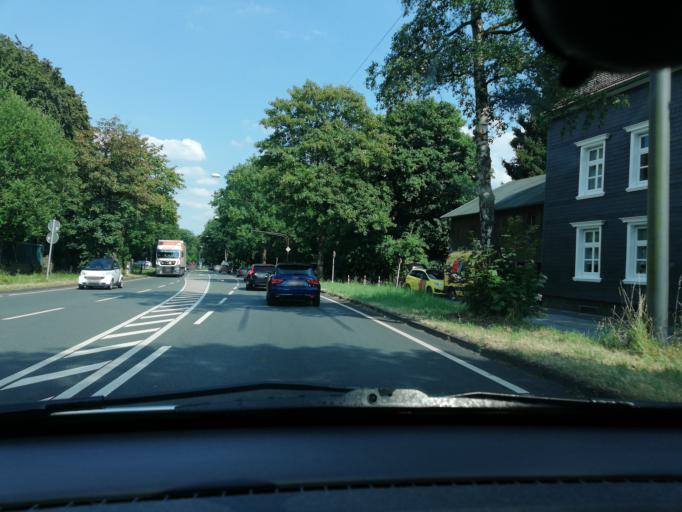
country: DE
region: North Rhine-Westphalia
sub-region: Regierungsbezirk Dusseldorf
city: Wuppertal
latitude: 51.2374
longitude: 7.1982
